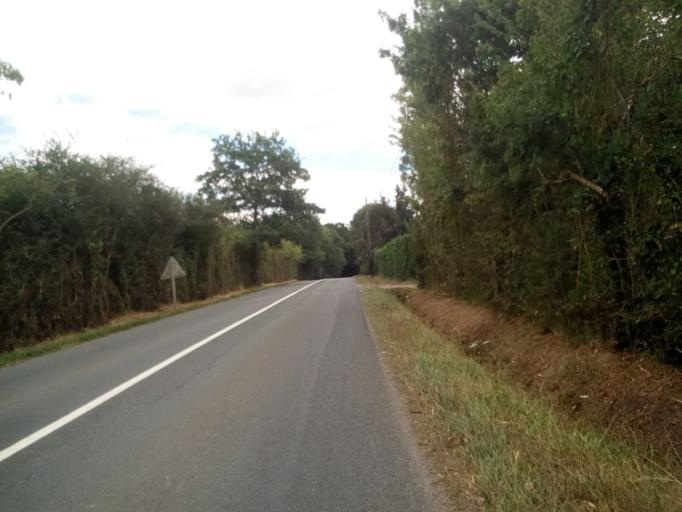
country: FR
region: Lower Normandy
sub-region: Departement du Calvados
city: Troarn
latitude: 49.1560
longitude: -0.1671
